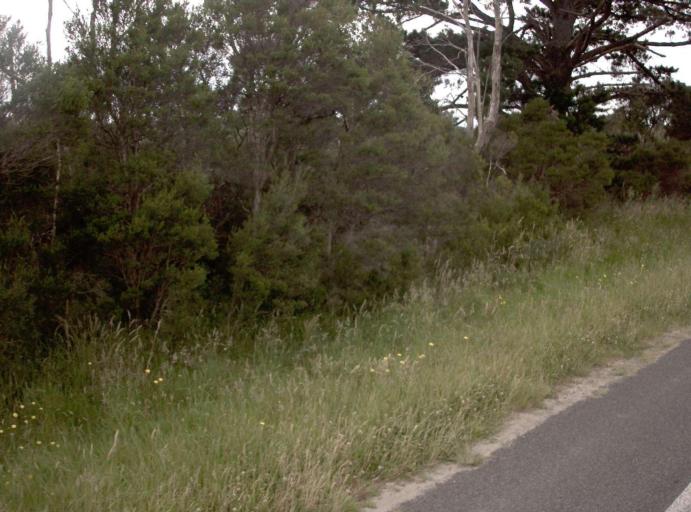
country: AU
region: Victoria
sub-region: Cardinia
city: Koo-Wee-Rup
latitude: -38.3282
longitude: 145.5913
